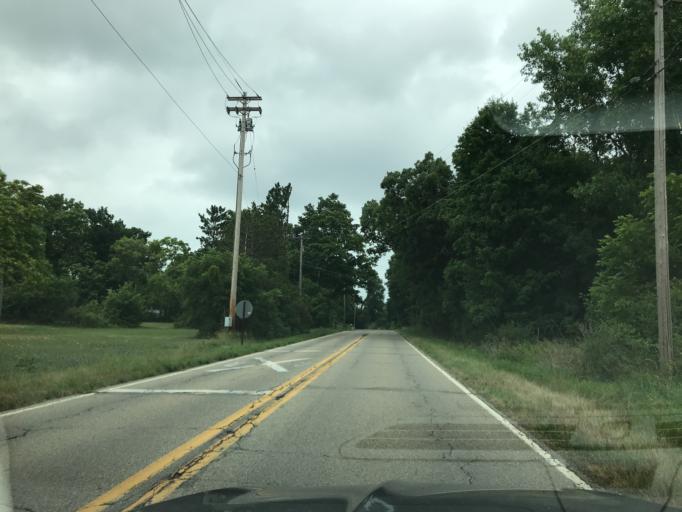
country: US
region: Michigan
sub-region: Eaton County
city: Waverly
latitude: 42.7742
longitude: -84.6475
